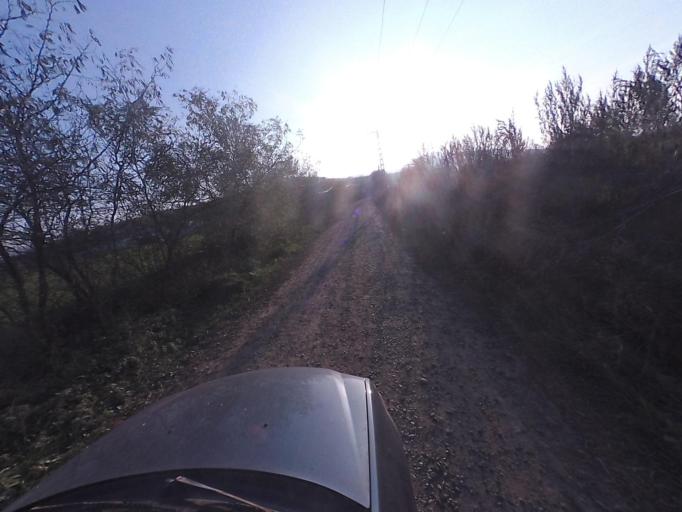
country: RO
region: Vaslui
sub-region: Comuna Bacesti
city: Bacesti
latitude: 46.8120
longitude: 27.2358
